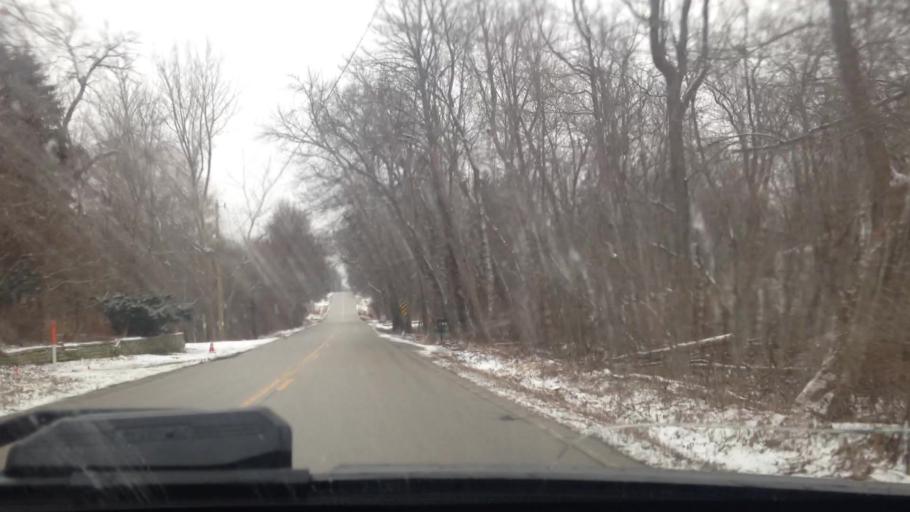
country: US
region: Wisconsin
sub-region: Waukesha County
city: Lannon
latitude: 43.1801
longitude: -88.1828
